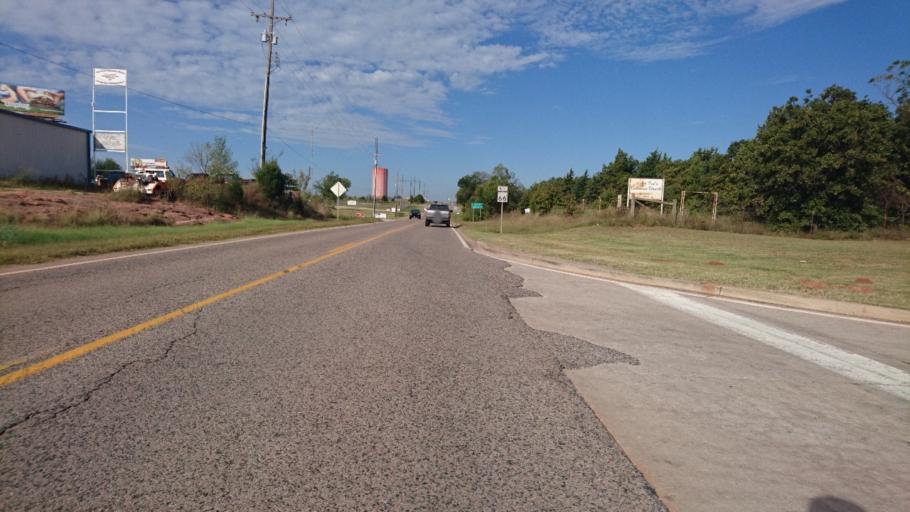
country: US
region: Oklahoma
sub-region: Oklahoma County
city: Luther
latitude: 35.6811
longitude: -97.0494
